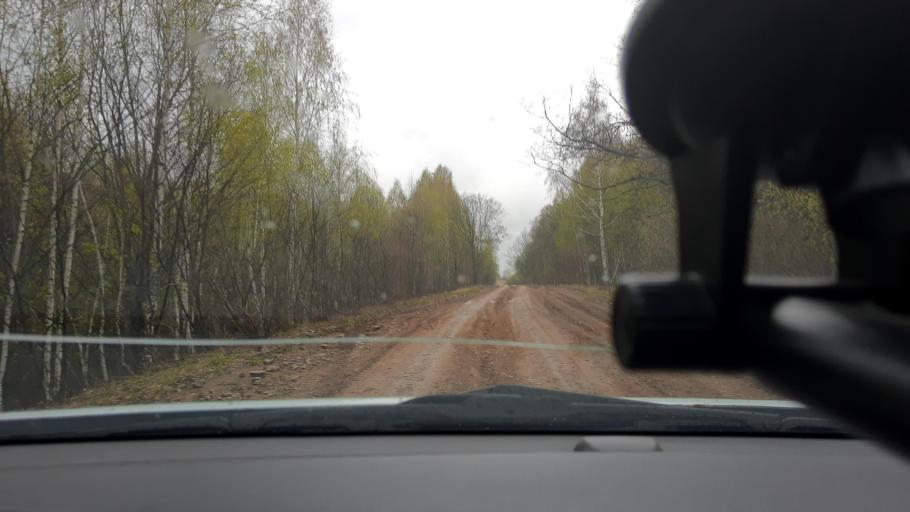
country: RU
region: Bashkortostan
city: Pavlovka
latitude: 55.4325
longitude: 56.3537
